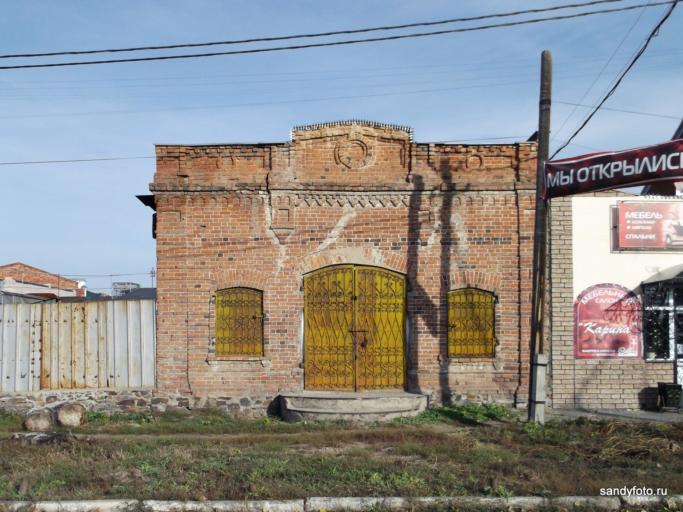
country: RU
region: Chelyabinsk
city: Troitsk
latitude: 54.0857
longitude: 61.5529
